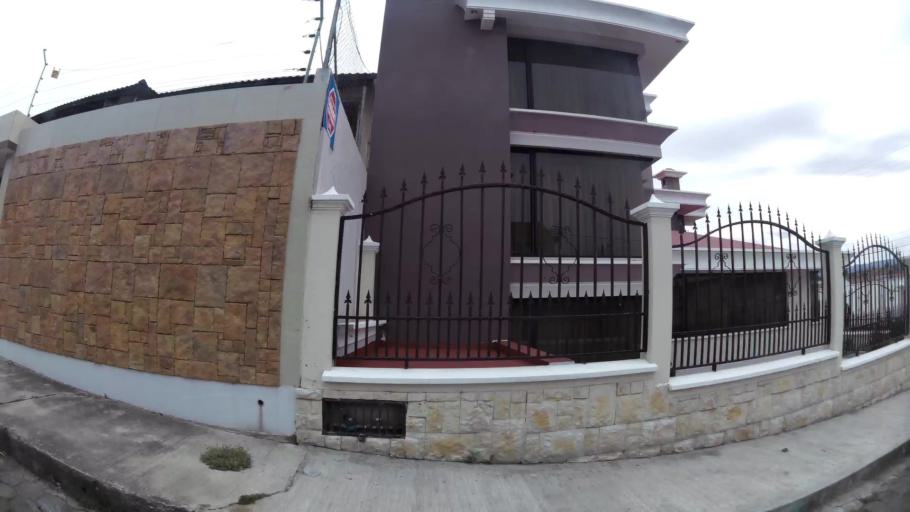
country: EC
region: Cotopaxi
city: Latacunga
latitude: -0.9463
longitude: -78.6127
